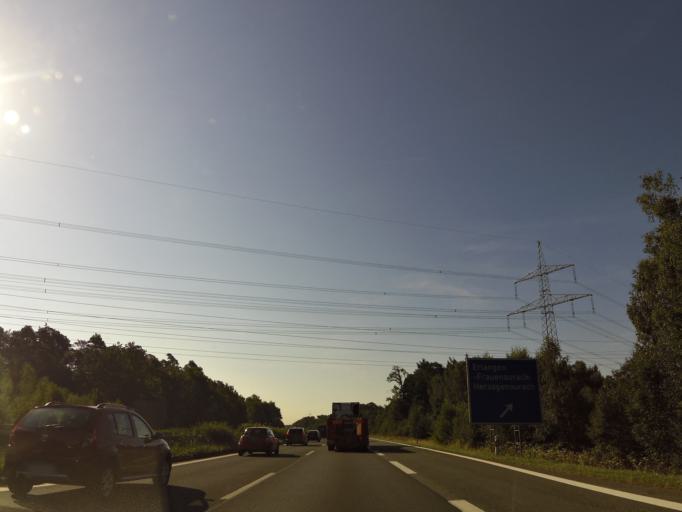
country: DE
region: Bavaria
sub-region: Regierungsbezirk Mittelfranken
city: Obermichelbach
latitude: 49.5703
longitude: 10.9376
